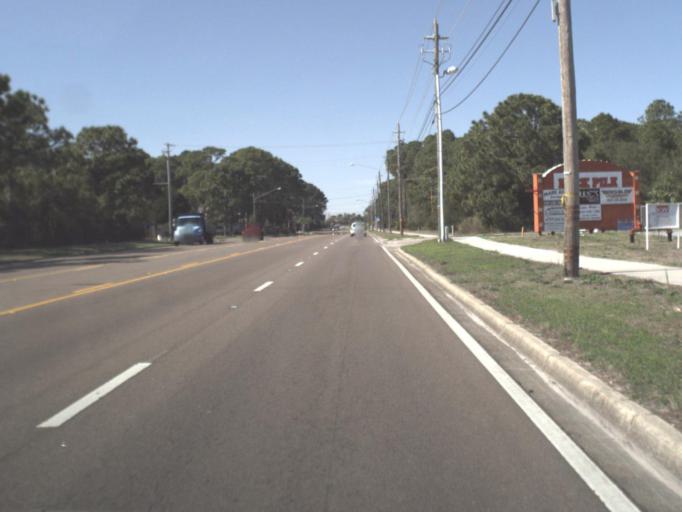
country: US
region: Florida
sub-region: Bay County
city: Panama City Beach
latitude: 30.1946
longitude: -85.8272
